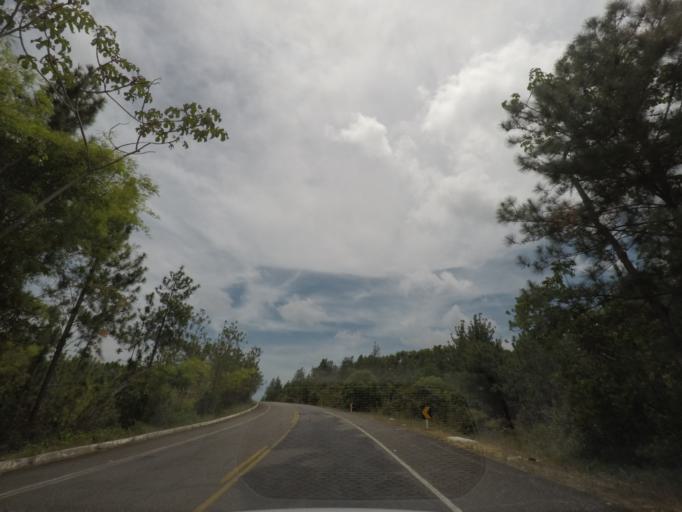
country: BR
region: Bahia
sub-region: Entre Rios
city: Entre Rios
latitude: -12.1303
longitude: -37.7919
